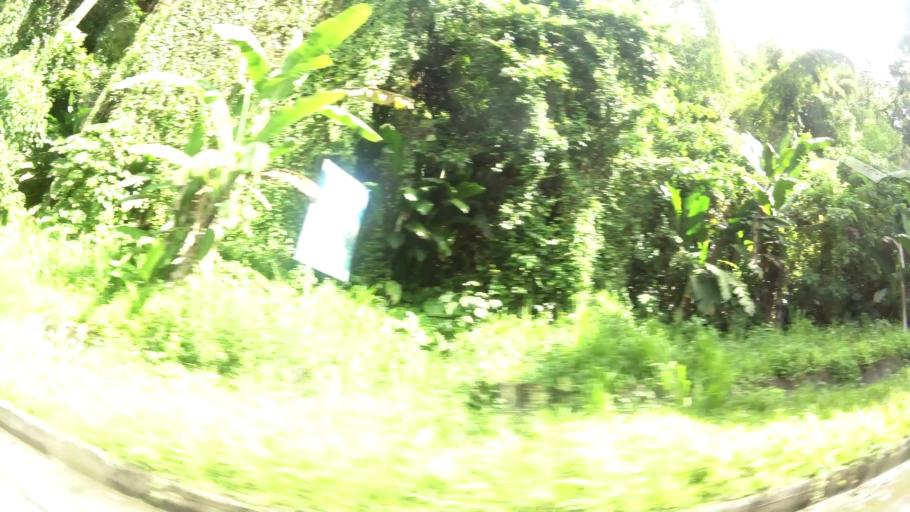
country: MQ
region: Martinique
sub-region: Martinique
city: Le Morne-Rouge
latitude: 14.7637
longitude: -61.1577
